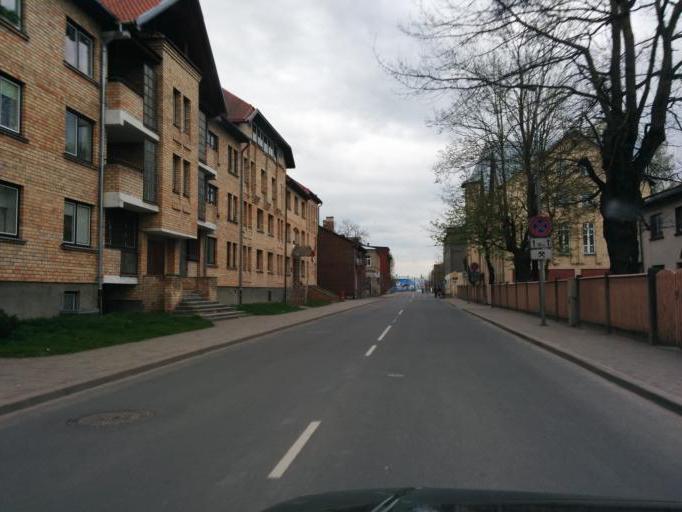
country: LV
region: Jelgava
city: Jelgava
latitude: 56.6425
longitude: 23.7239
